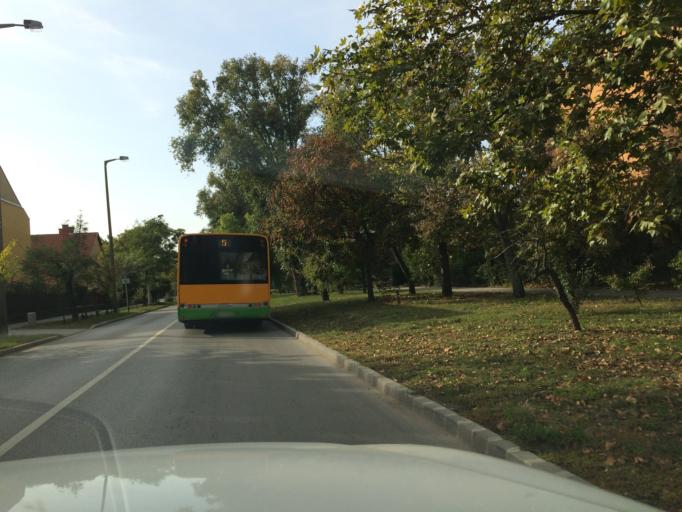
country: HU
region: Szabolcs-Szatmar-Bereg
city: Nyiregyhaza
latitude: 47.9788
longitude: 21.7273
